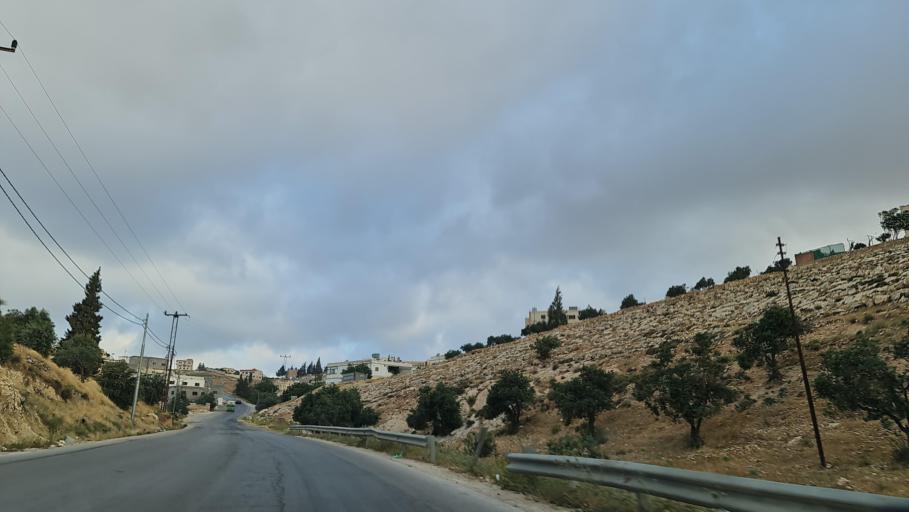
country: JO
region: Amman
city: Al Jubayhah
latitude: 32.0921
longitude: 35.9093
